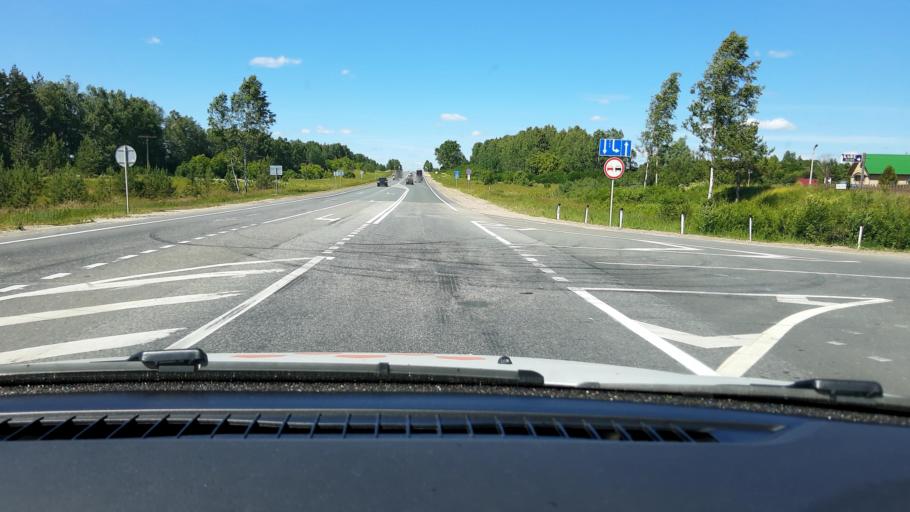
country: RU
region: Nizjnij Novgorod
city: Dal'neye Konstantinovo
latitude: 55.9594
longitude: 43.9757
